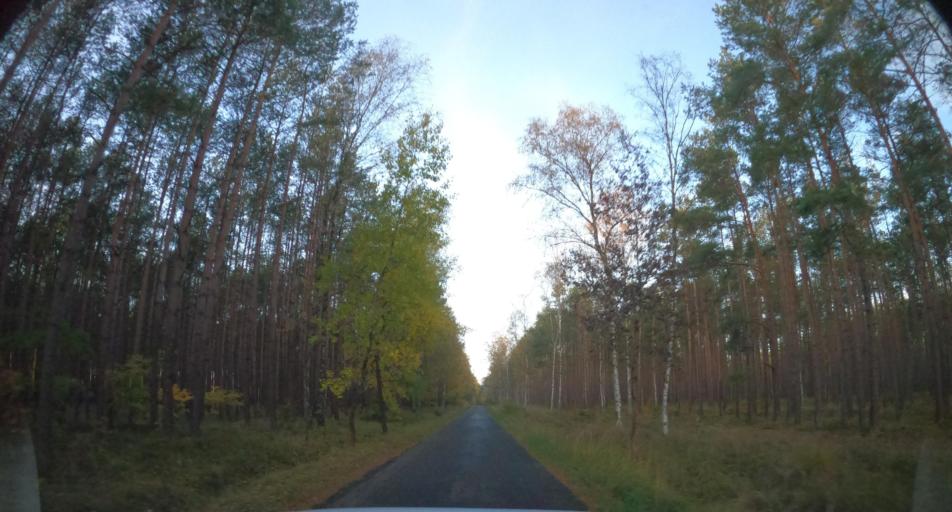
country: PL
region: West Pomeranian Voivodeship
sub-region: Powiat policki
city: Nowe Warpno
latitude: 53.6425
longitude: 14.4042
